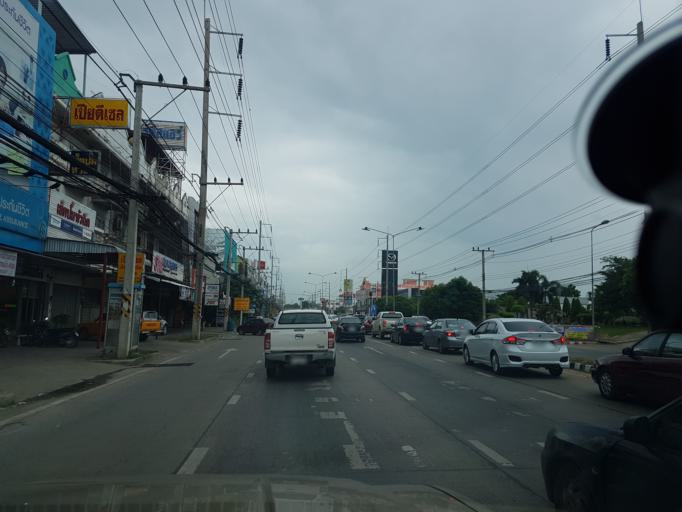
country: TH
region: Lop Buri
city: Lop Buri
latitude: 14.7964
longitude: 100.6650
